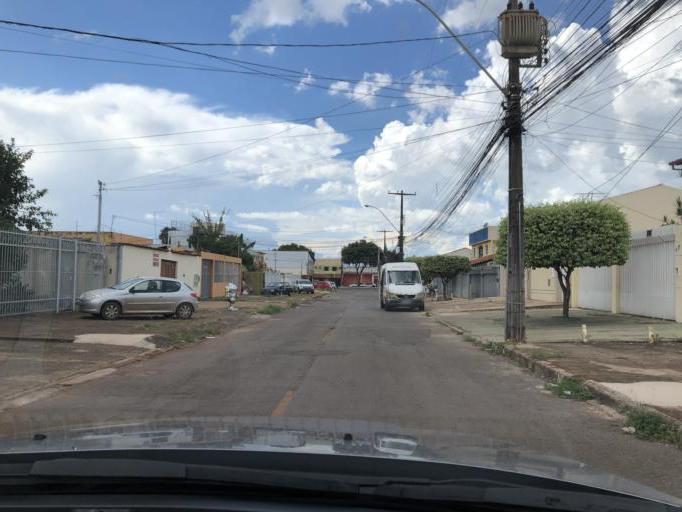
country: BR
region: Federal District
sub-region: Brasilia
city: Brasilia
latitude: -15.8029
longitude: -48.0625
